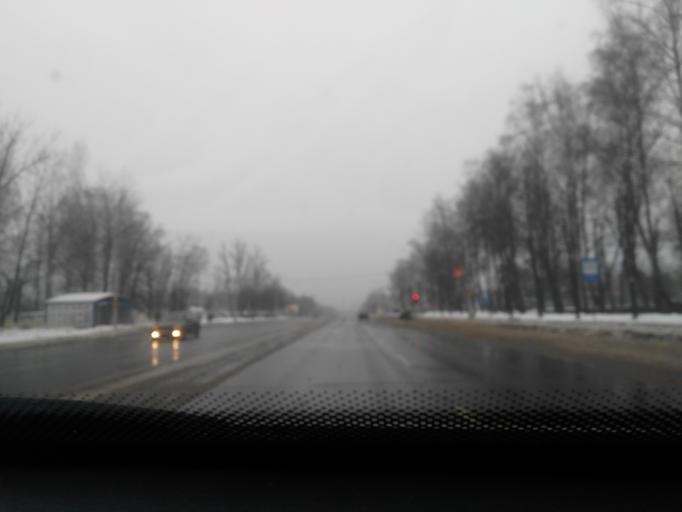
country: BY
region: Mogilev
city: Babruysk
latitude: 53.1727
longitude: 29.2027
